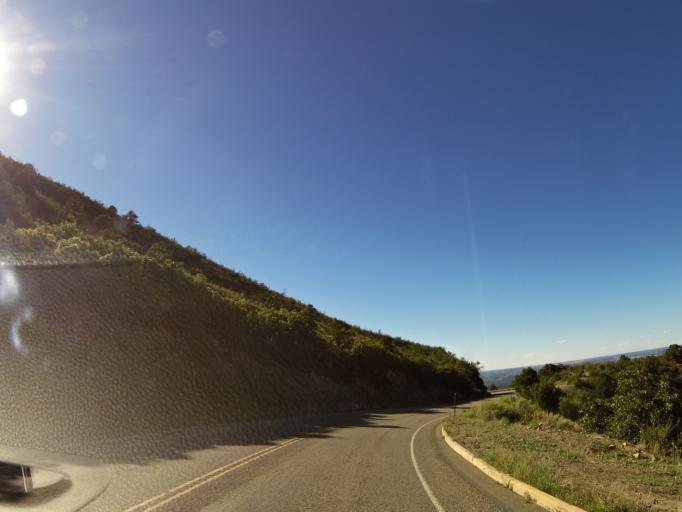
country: US
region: Colorado
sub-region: Montezuma County
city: Mancos
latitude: 37.3185
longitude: -108.4161
